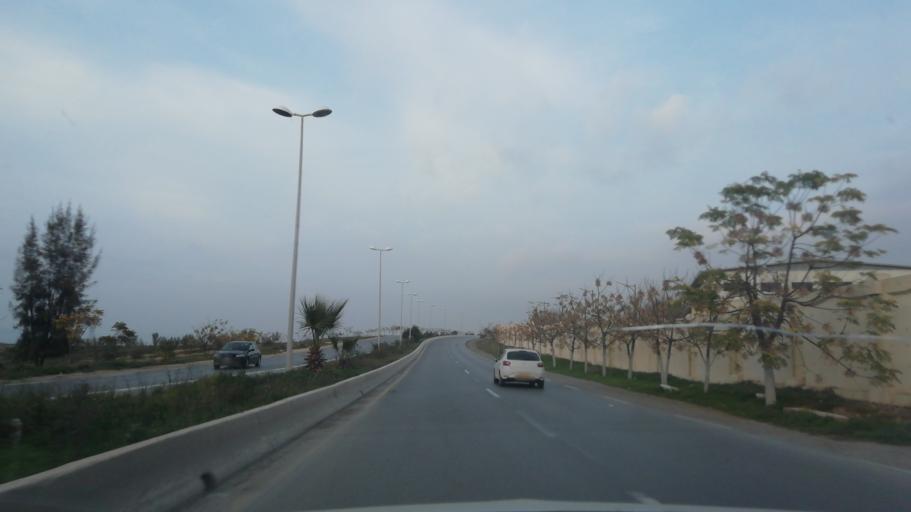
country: DZ
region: Sidi Bel Abbes
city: Sidi Bel Abbes
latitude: 35.2211
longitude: -0.6463
